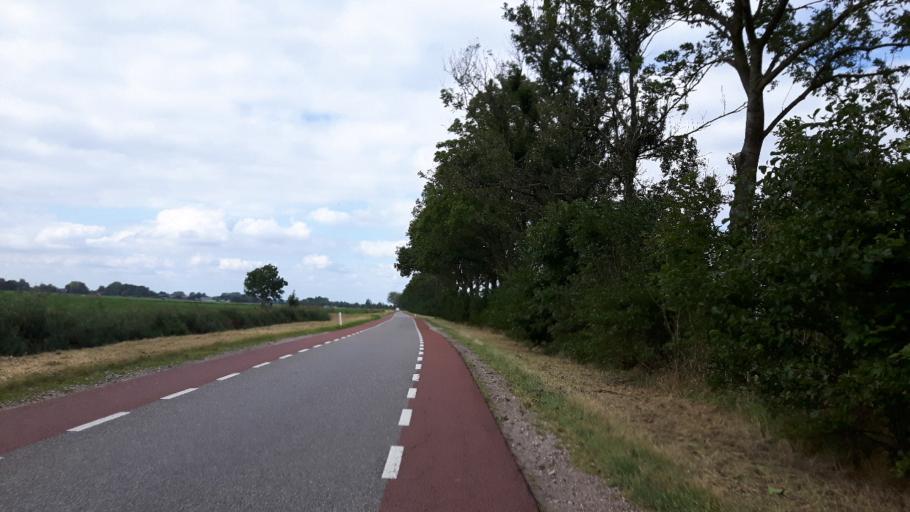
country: NL
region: Utrecht
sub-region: Stichtse Vecht
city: Breukelen
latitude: 52.1754
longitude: 4.9673
